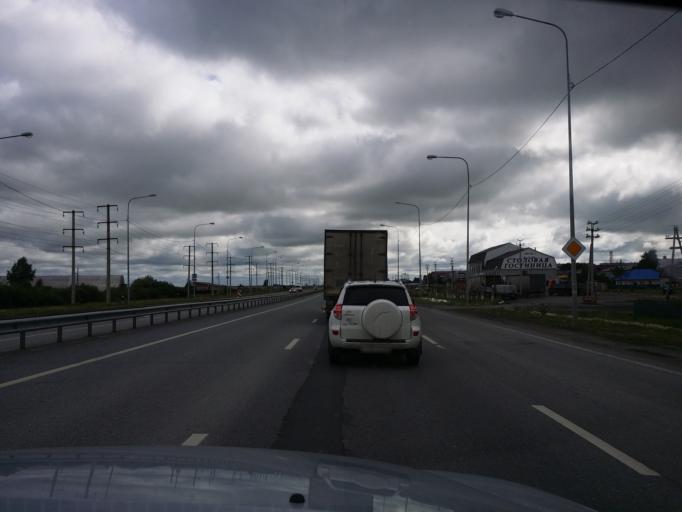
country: RU
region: Tjumen
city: Antipino
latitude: 57.1776
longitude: 65.9178
